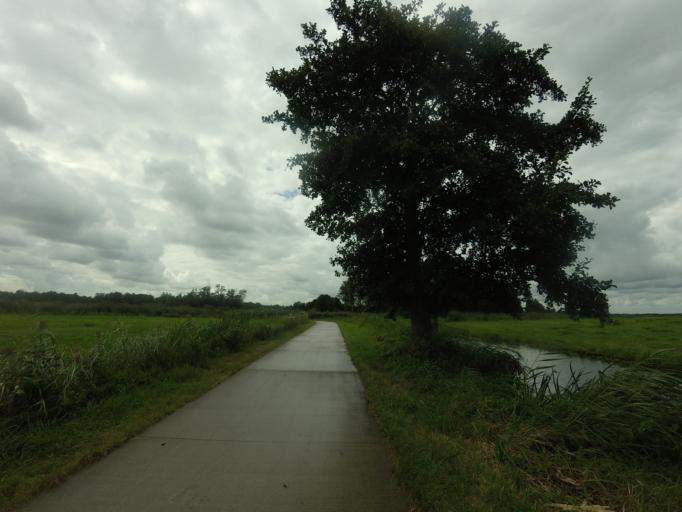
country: NL
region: Overijssel
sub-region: Gemeente Steenwijkerland
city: Wanneperveen
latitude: 52.7204
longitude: 6.1288
